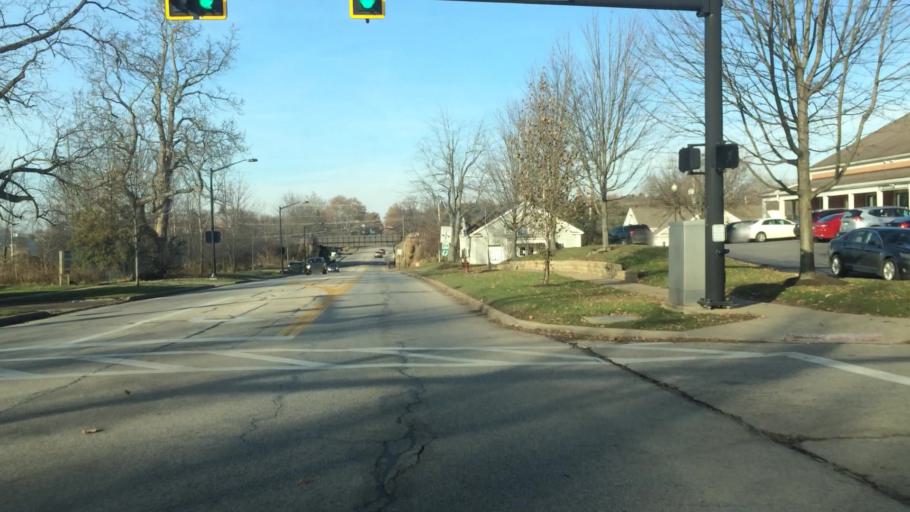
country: US
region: Ohio
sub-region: Summit County
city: Hudson
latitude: 41.2361
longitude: -81.4404
